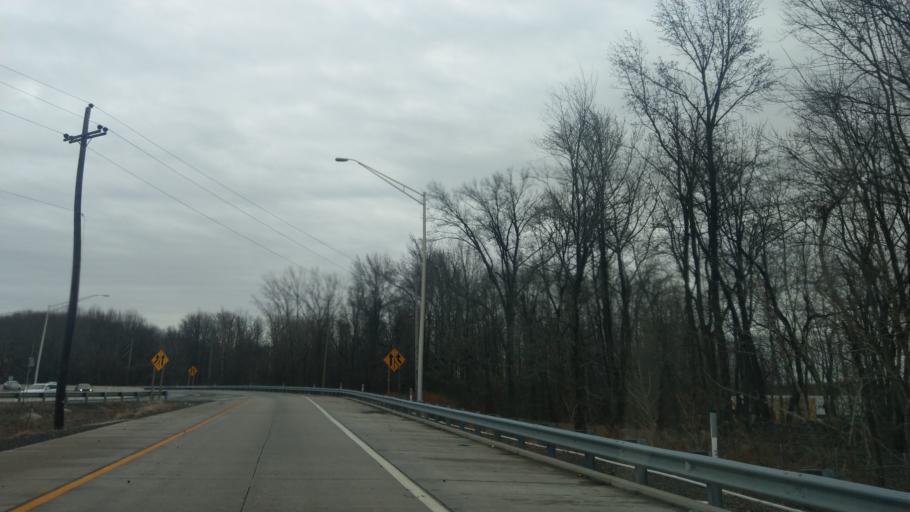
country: US
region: Pennsylvania
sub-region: Bucks County
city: Bristol
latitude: 40.1226
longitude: -74.8548
